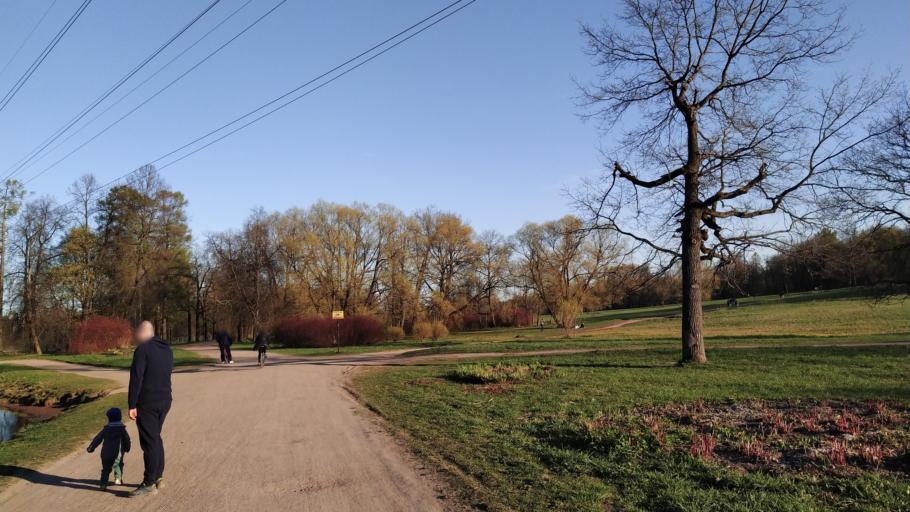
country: RU
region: St.-Petersburg
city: Pushkin
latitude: 59.7113
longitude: 30.4207
